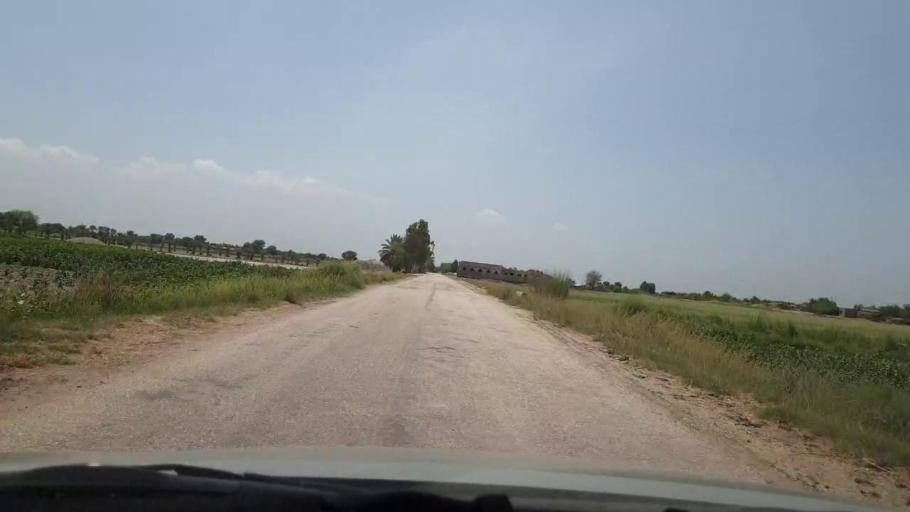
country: PK
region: Sindh
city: Pano Aqil
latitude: 27.6636
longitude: 69.1151
